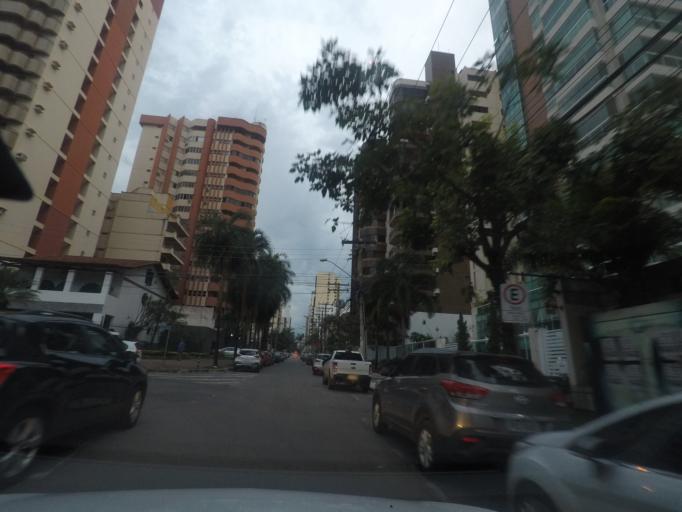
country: BR
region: Goias
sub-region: Goiania
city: Goiania
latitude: -16.7124
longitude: -49.2660
